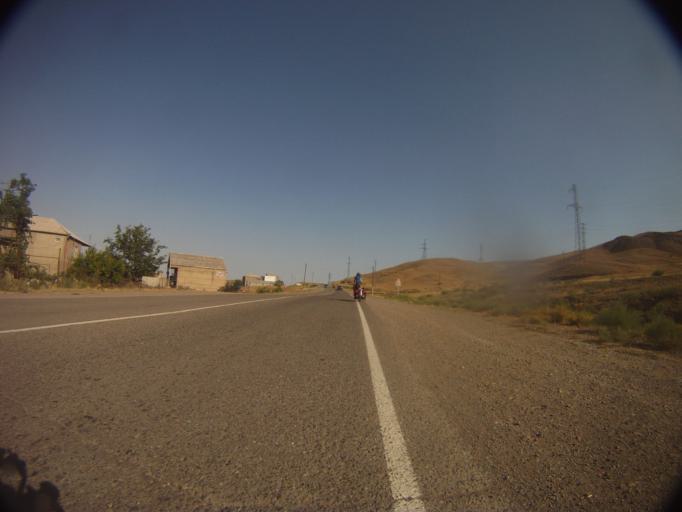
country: GE
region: Kvemo Kartli
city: Rust'avi
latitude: 41.5510
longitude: 44.9739
